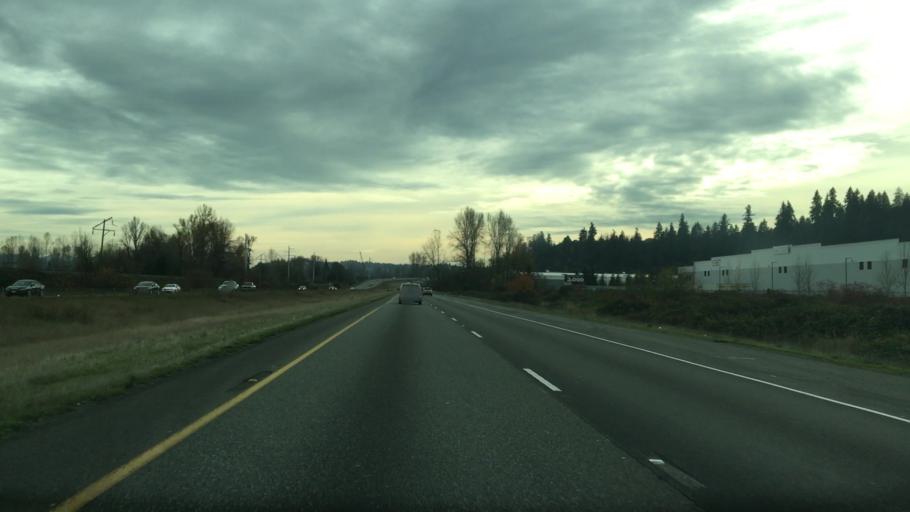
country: US
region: Washington
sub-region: Pierce County
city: Sumner
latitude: 47.2165
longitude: -122.2473
